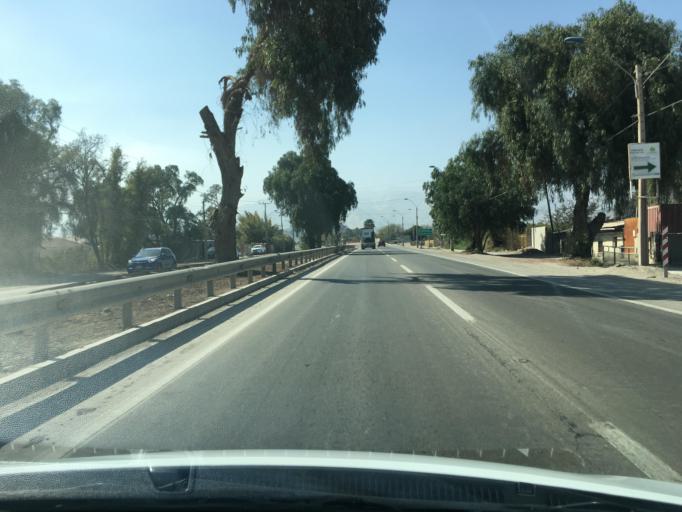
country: CL
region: Atacama
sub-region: Provincia de Copiapo
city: Copiapo
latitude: -27.4122
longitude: -70.2867
